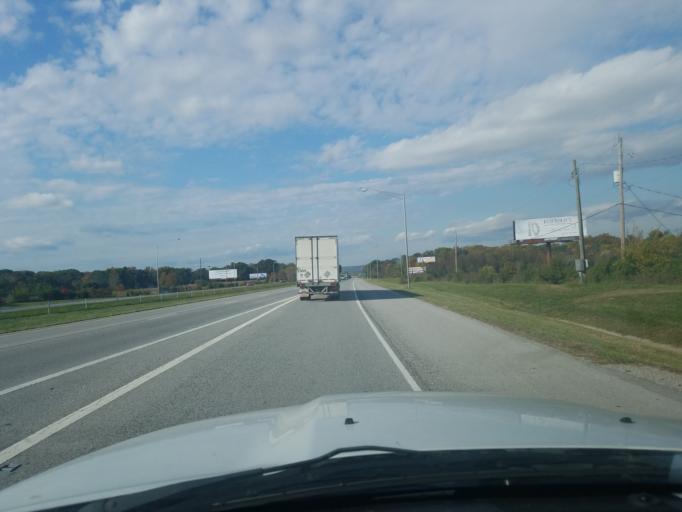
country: US
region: Indiana
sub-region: Clark County
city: Clarksville
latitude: 38.3458
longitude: -85.7607
